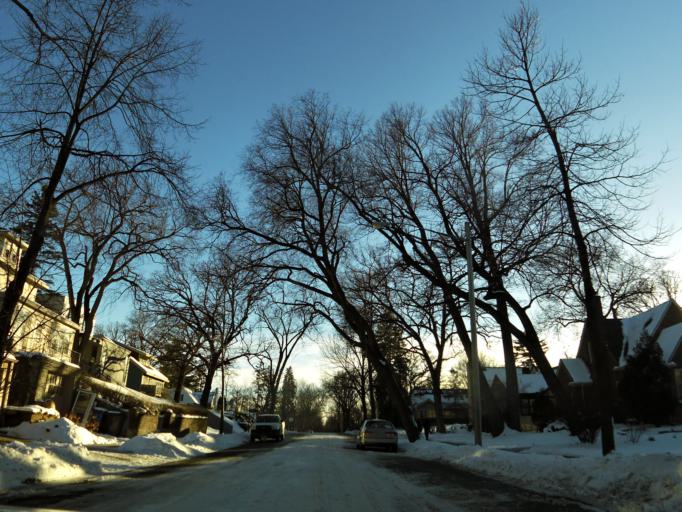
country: US
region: Minnesota
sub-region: Hennepin County
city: Saint Louis Park
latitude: 44.9295
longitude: -93.3227
